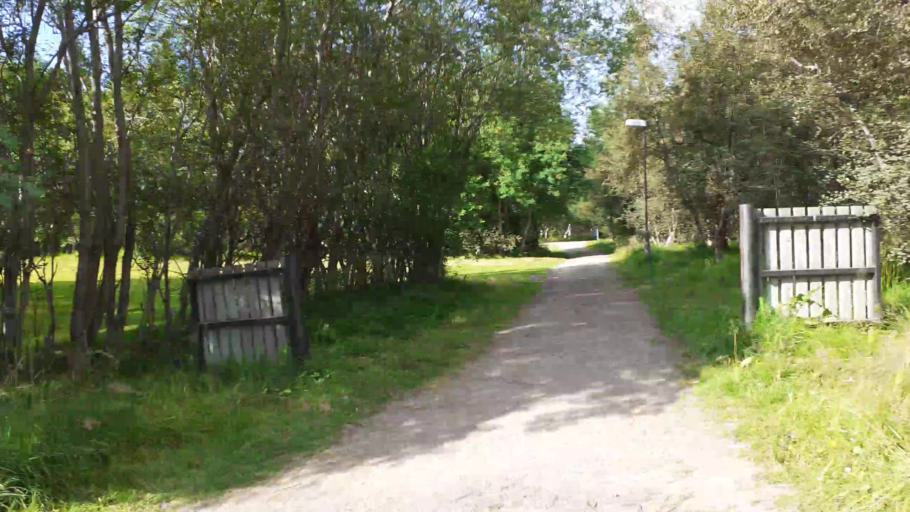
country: IS
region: Northeast
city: Akureyri
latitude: 65.6450
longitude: -18.0855
